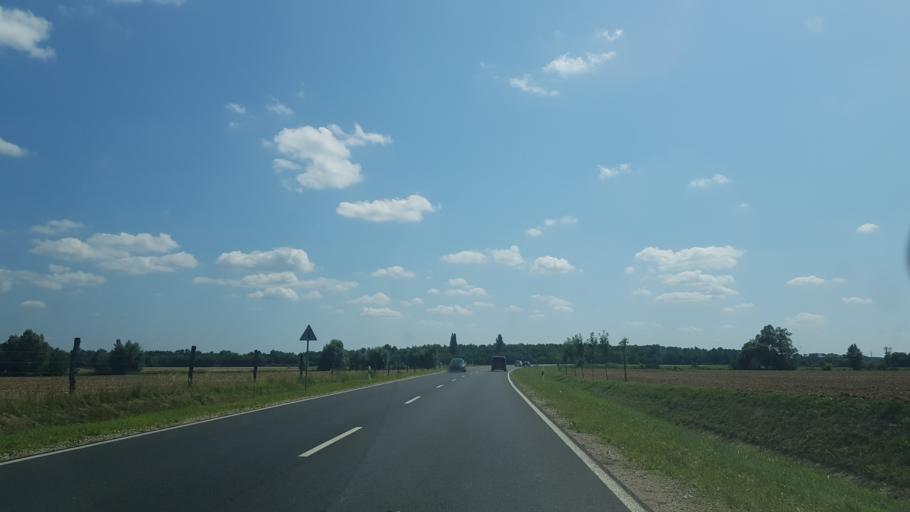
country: HU
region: Somogy
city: Marcali
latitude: 46.5746
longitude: 17.4300
